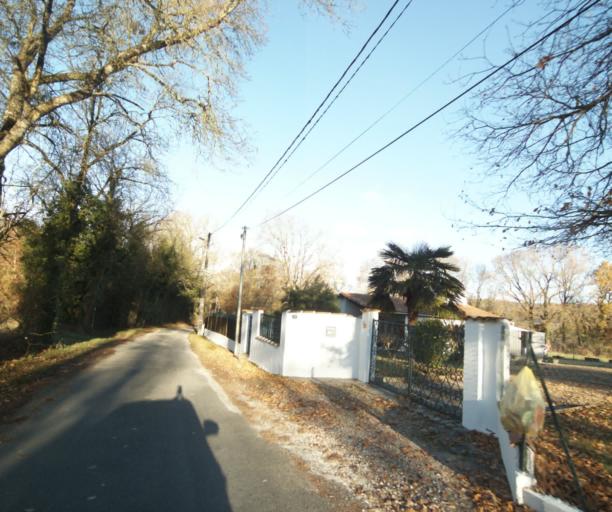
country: FR
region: Poitou-Charentes
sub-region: Departement de la Charente-Maritime
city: Fontcouverte
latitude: 45.7532
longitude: -0.6067
